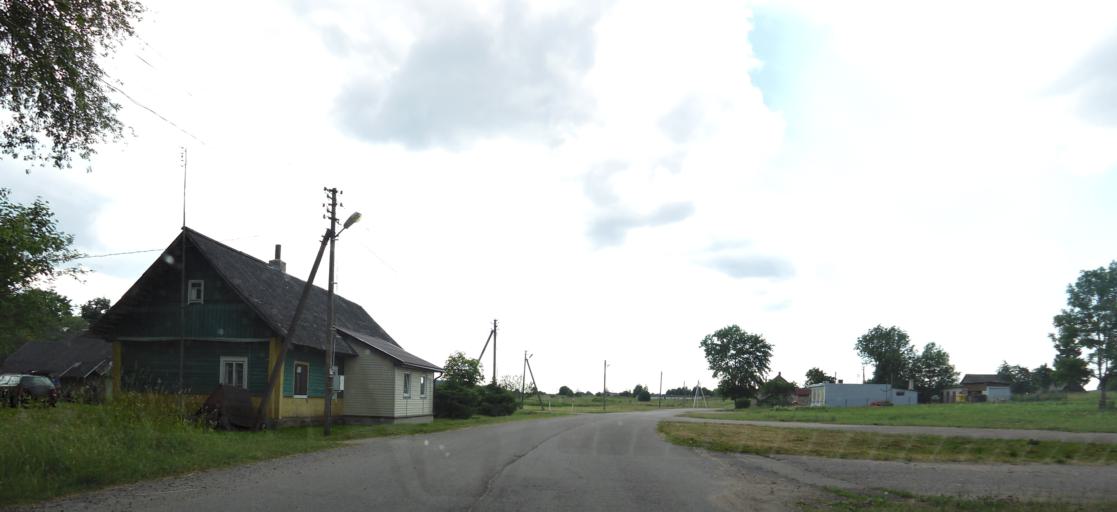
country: LT
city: Skaidiskes
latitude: 54.5411
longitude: 25.6534
